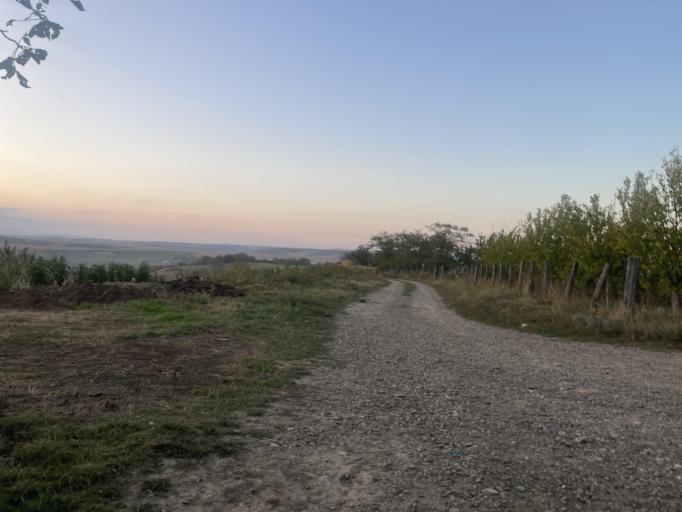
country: RO
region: Iasi
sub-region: Comuna Dumesti
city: Pausesti
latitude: 47.1516
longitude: 27.3166
